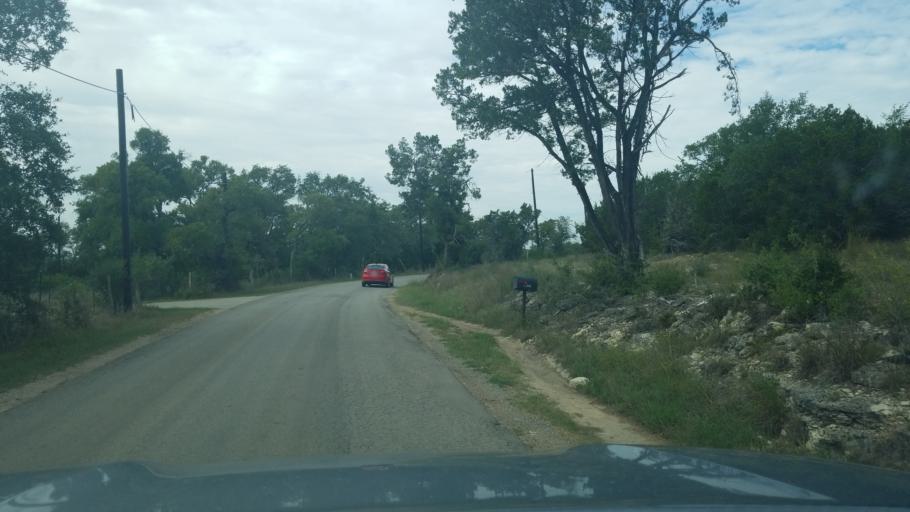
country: US
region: Texas
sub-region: Comal County
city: Bulverde
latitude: 29.7749
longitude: -98.4128
